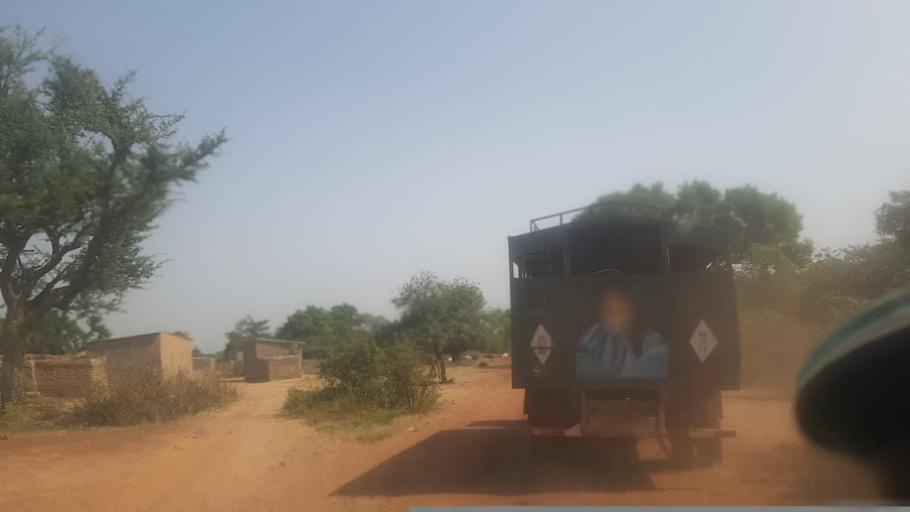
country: ML
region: Segou
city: Bla
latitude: 12.9131
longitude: -6.2466
